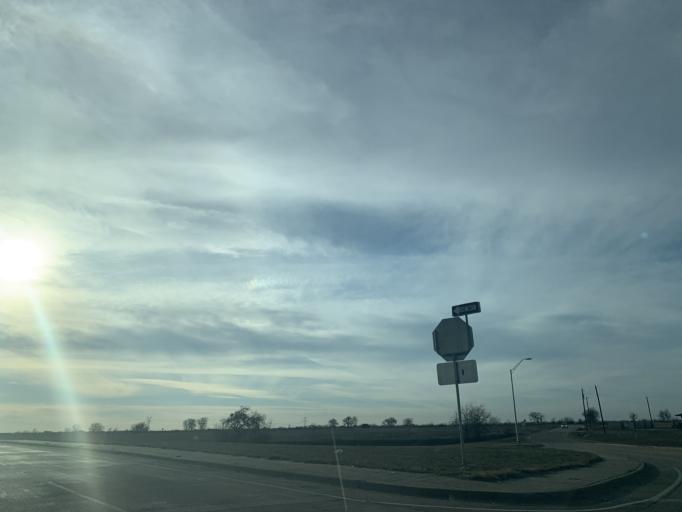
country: US
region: Texas
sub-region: Bell County
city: Salado
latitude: 30.9788
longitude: -97.5117
